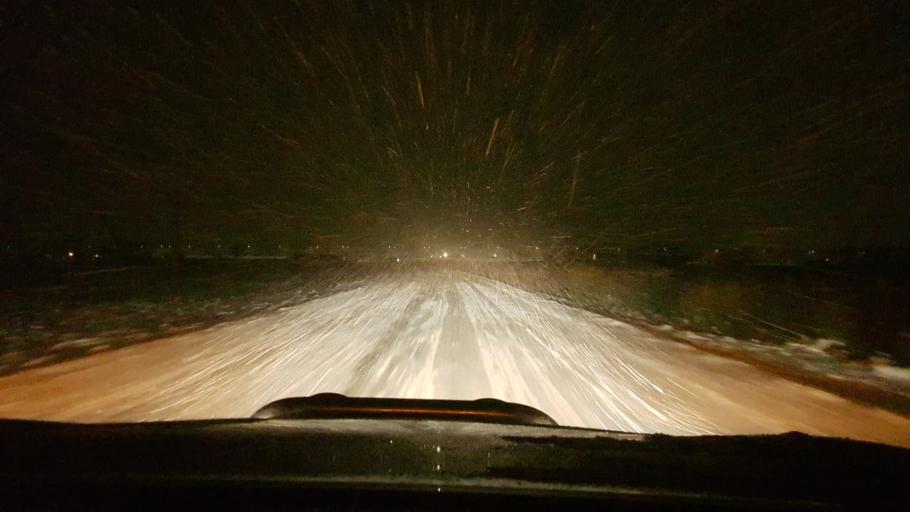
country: EE
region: Harju
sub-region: Kuusalu vald
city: Kuusalu
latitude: 59.4388
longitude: 25.3836
